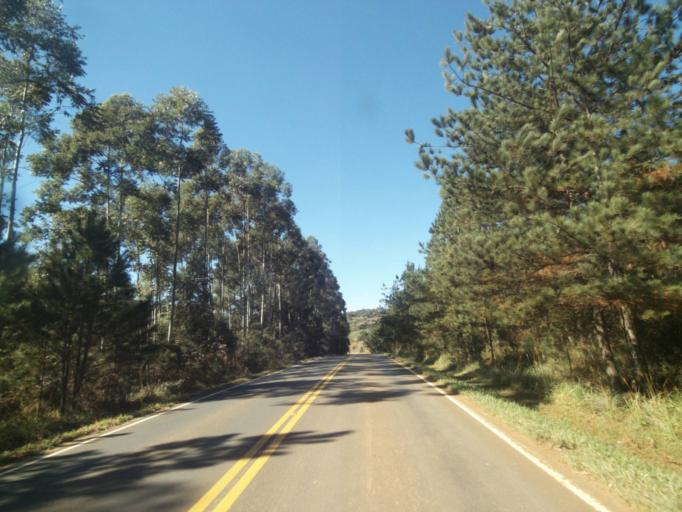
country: BR
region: Parana
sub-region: Tibagi
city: Tibagi
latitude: -24.4975
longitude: -50.4588
